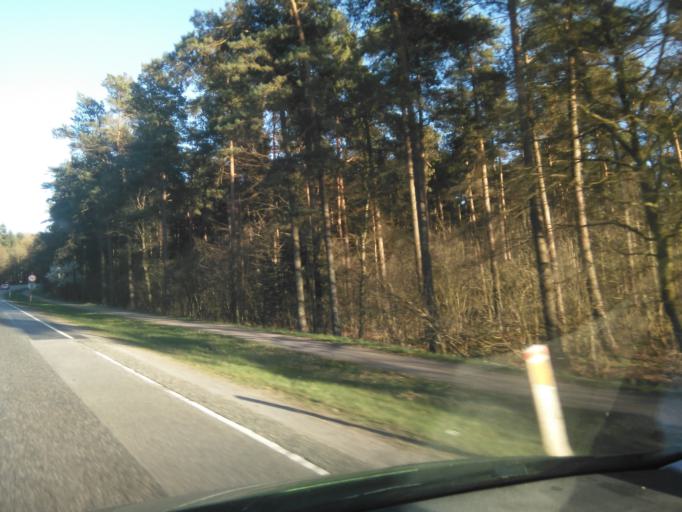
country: DK
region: Central Jutland
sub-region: Silkeborg Kommune
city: Svejbaek
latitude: 56.1615
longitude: 9.6163
